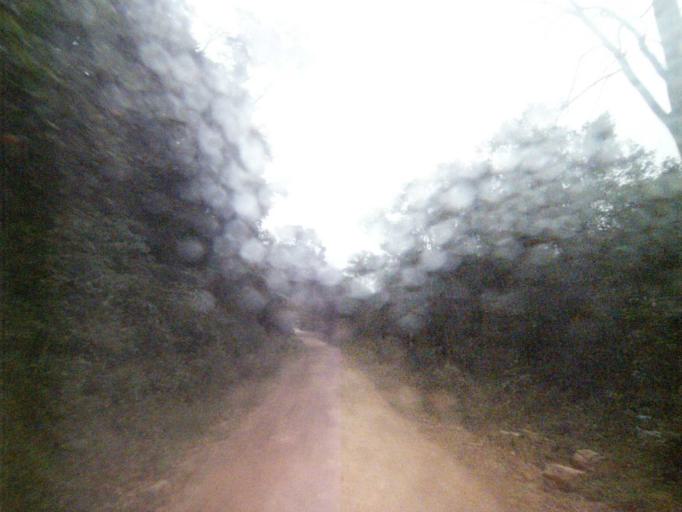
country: BR
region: Santa Catarina
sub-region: Anitapolis
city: Anitapolis
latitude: -27.8688
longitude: -49.1312
